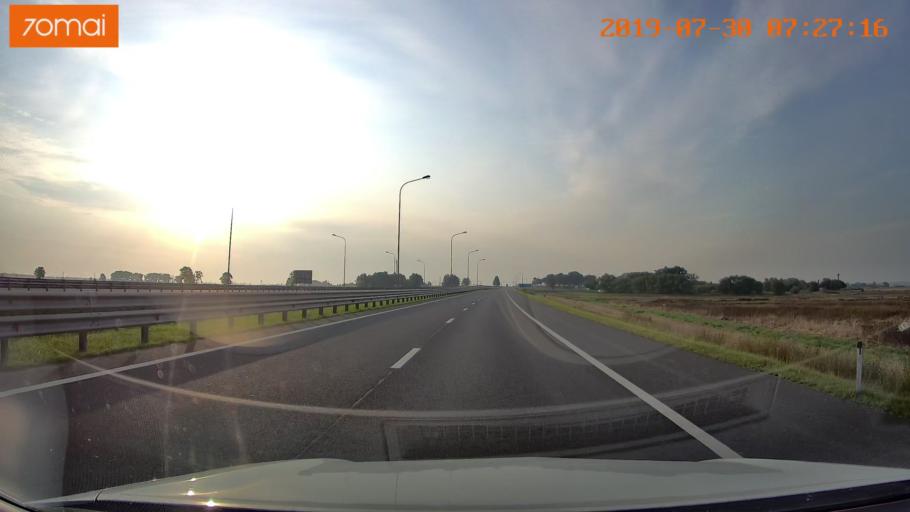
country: RU
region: Kaliningrad
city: Gvardeysk
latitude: 54.6831
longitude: 20.8825
